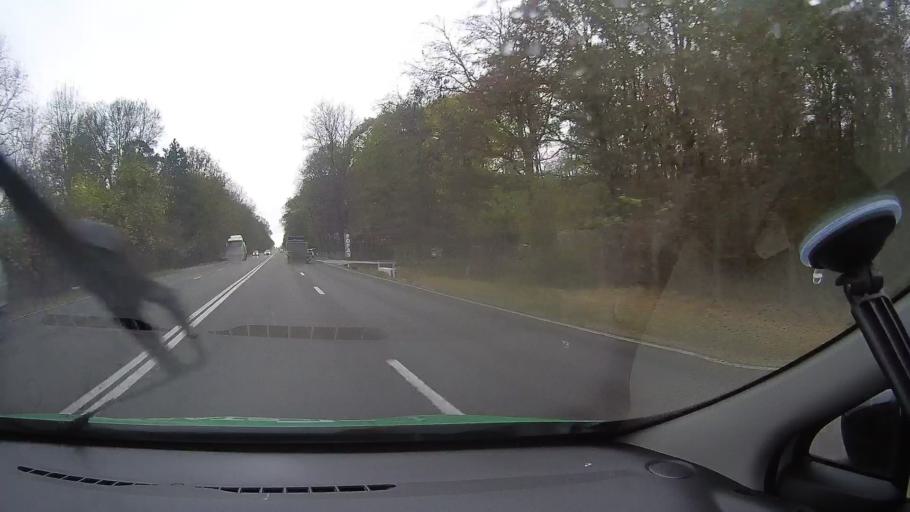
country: RO
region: Constanta
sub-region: Comuna Valu lui Traian
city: Valu lui Traian
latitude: 44.1652
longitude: 28.5021
